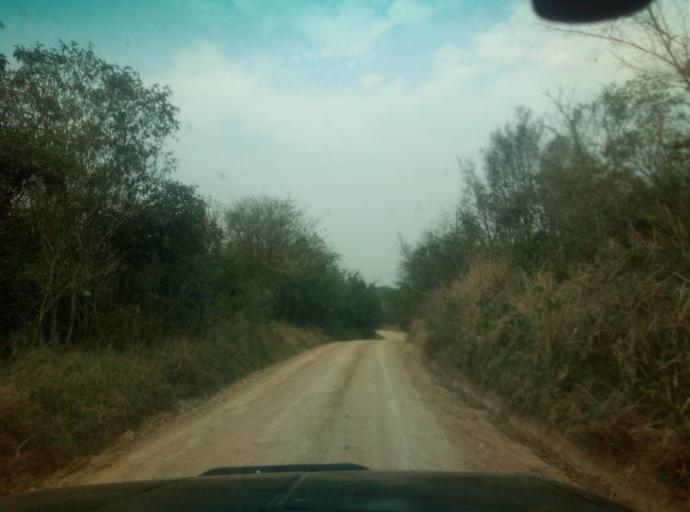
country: PY
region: Caaguazu
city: San Joaquin
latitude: -25.0975
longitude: -56.1394
